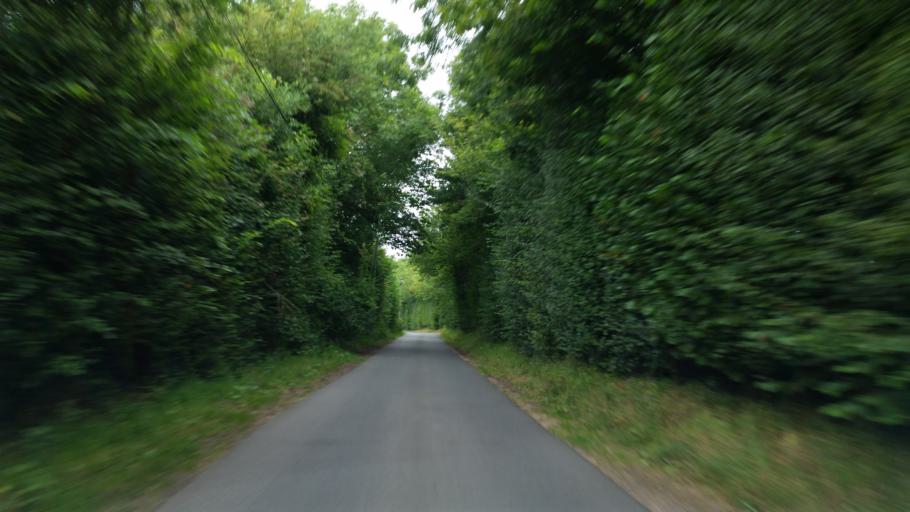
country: FR
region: Lower Normandy
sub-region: Departement du Calvados
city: Equemauville
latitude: 49.3987
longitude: 0.2278
